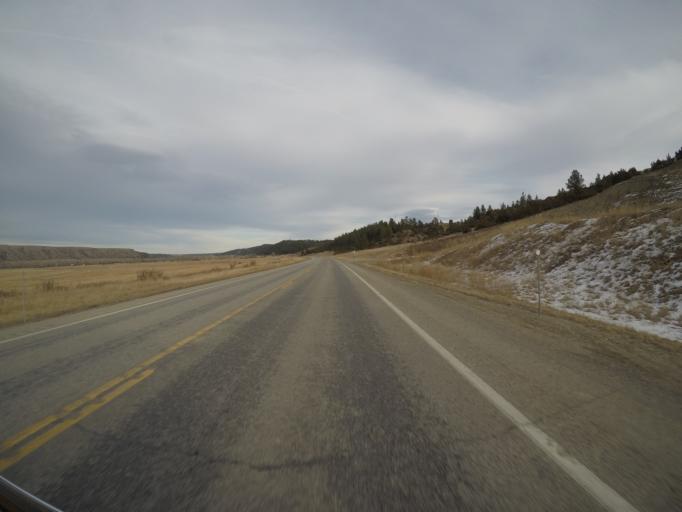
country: US
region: Montana
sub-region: Stillwater County
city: Absarokee
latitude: 45.5445
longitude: -109.3811
